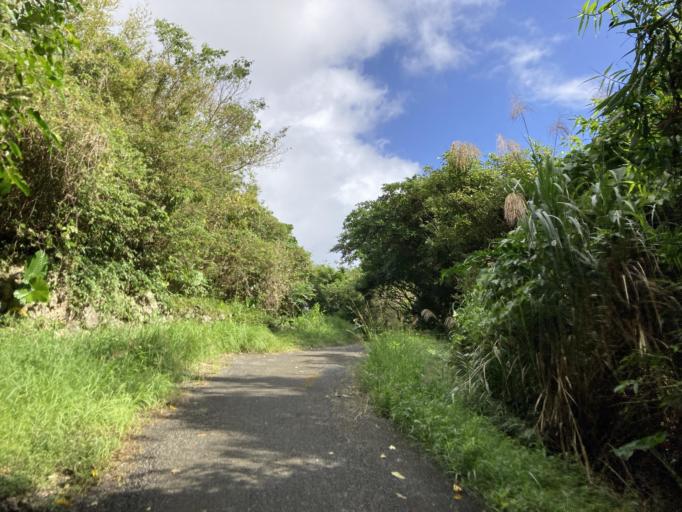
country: JP
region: Okinawa
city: Ginowan
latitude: 26.1611
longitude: 127.8126
